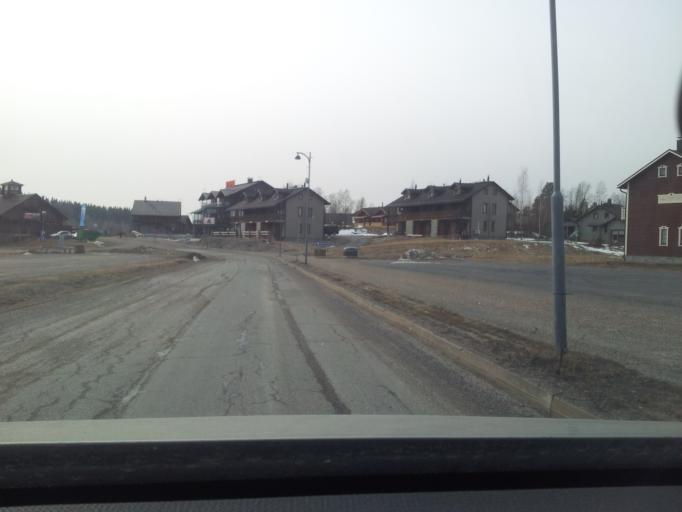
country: FI
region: Central Finland
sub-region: Jaemsae
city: Jaemsae
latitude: 61.8808
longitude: 25.3006
